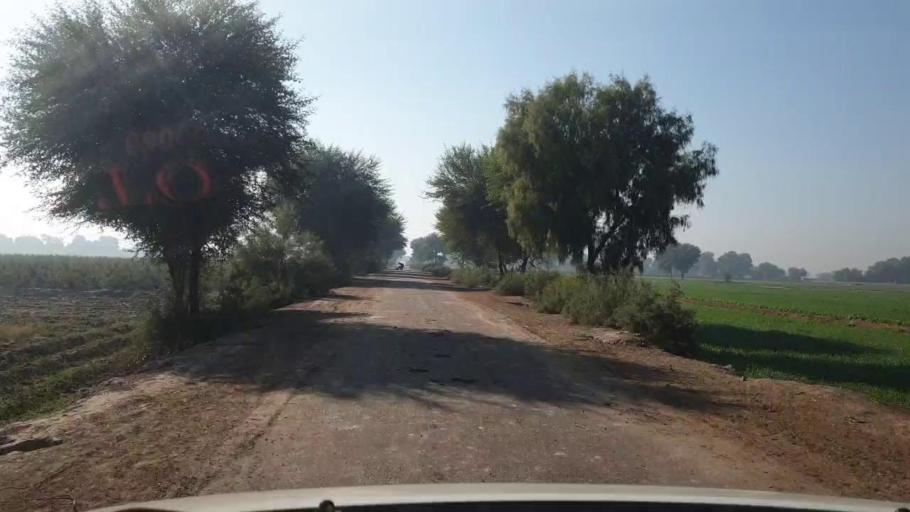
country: PK
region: Sindh
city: Dadu
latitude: 26.6436
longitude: 67.8213
